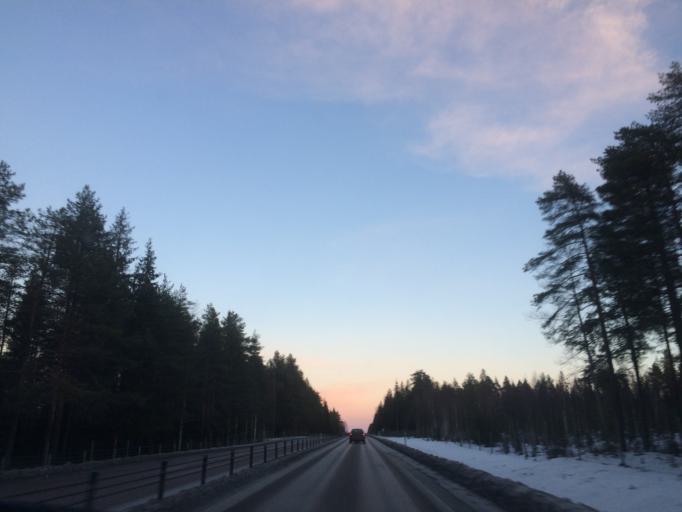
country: SE
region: Norrbotten
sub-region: Lulea Kommun
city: Ranea
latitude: 65.8270
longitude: 22.2303
